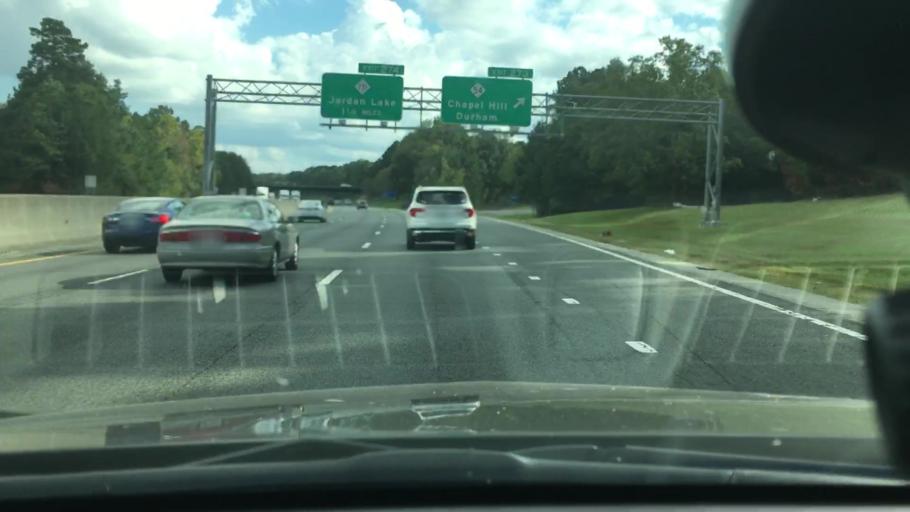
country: US
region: North Carolina
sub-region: Orange County
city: Chapel Hill
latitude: 35.9163
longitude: -78.9843
